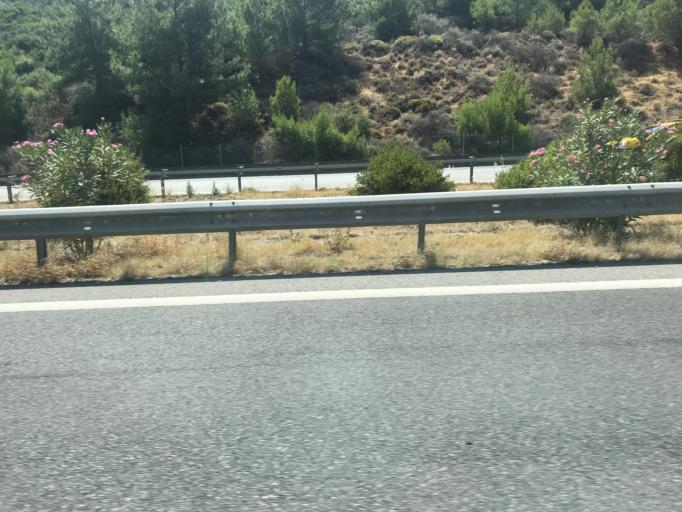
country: TR
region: Izmir
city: Urla
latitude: 38.3460
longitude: 26.8335
